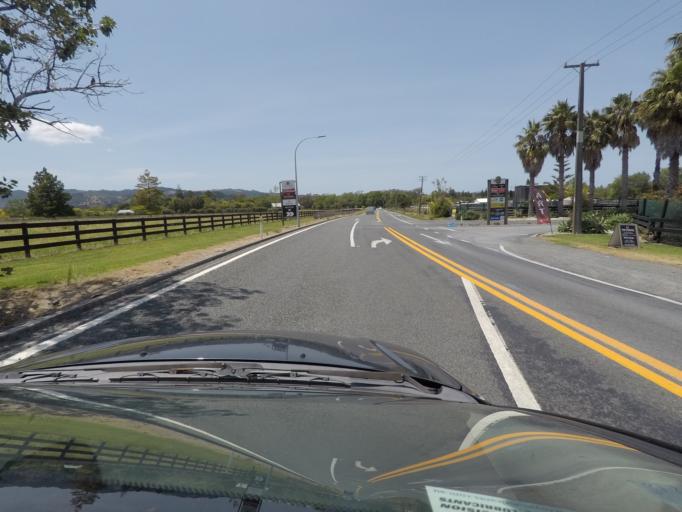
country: NZ
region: Auckland
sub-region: Auckland
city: Warkworth
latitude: -36.3421
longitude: 174.7330
